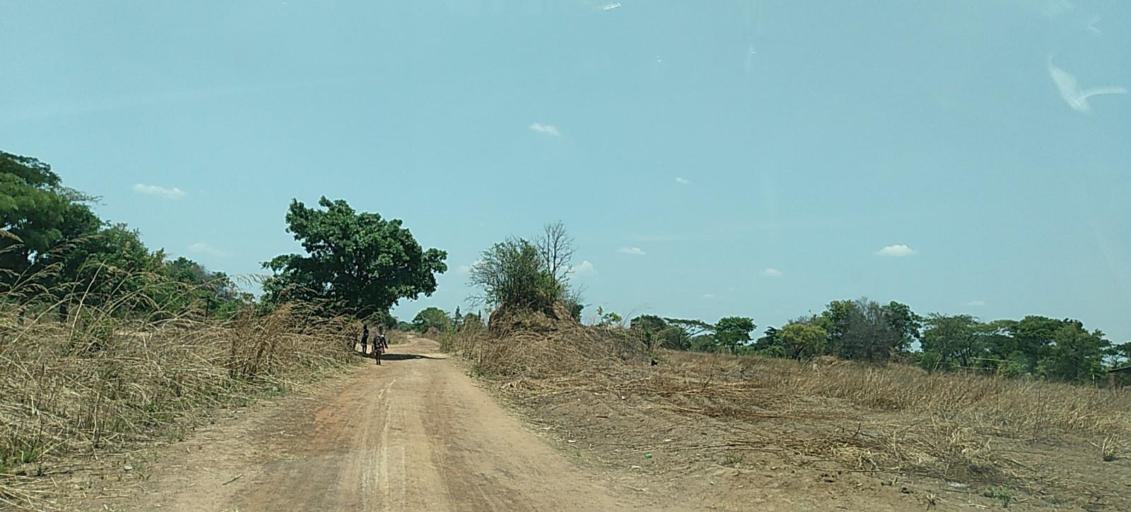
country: ZM
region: Copperbelt
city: Luanshya
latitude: -13.0898
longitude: 28.4062
